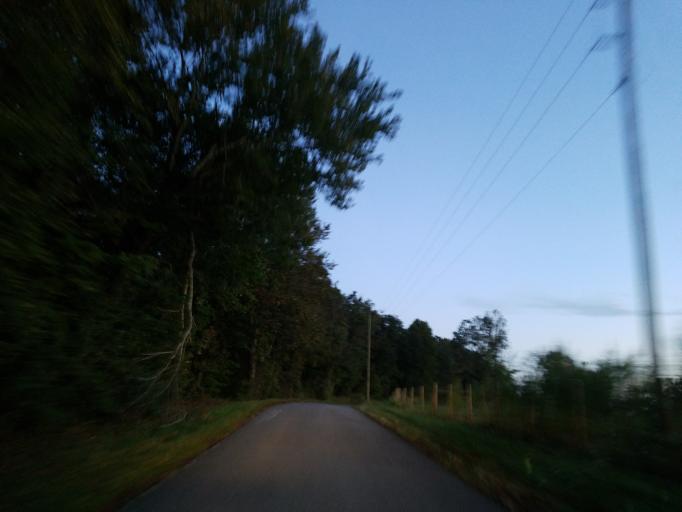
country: US
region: Georgia
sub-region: Dawson County
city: Dawsonville
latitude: 34.5268
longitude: -84.1769
